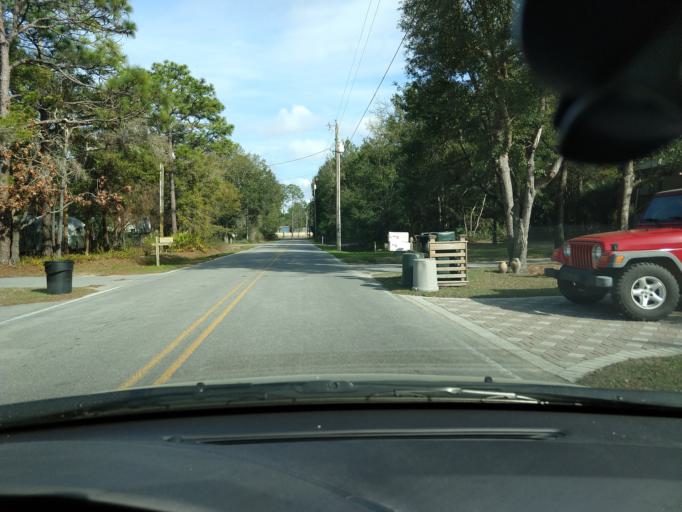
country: US
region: Florida
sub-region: Walton County
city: Seaside
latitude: 30.3761
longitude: -86.1557
